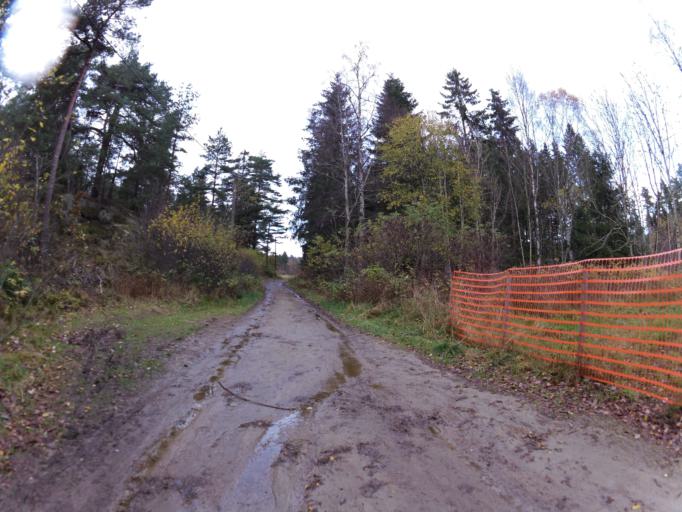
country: NO
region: Ostfold
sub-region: Fredrikstad
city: Fredrikstad
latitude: 59.2398
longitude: 10.9424
